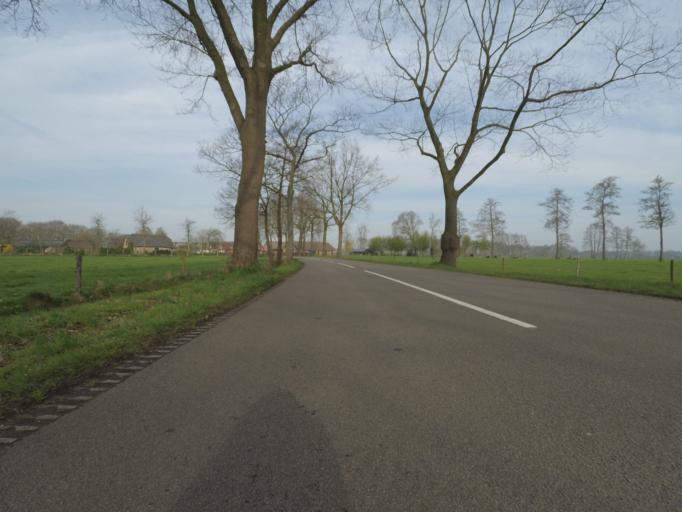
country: NL
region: Gelderland
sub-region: Gemeente Barneveld
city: Kootwijkerbroek
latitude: 52.1650
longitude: 5.6734
